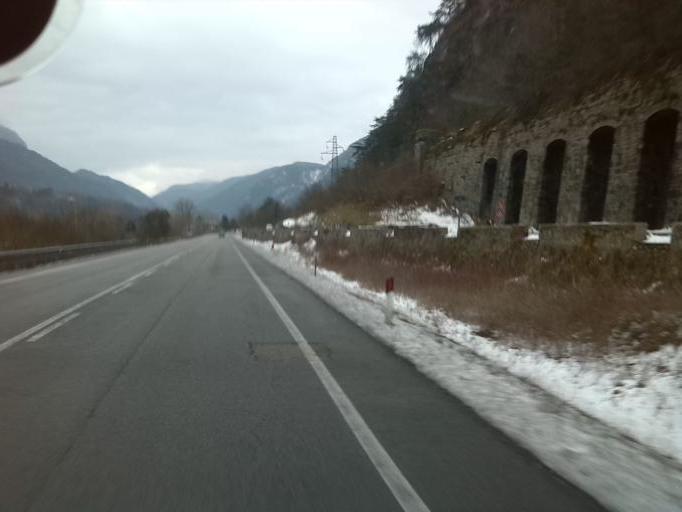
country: IT
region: Friuli Venezia Giulia
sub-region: Provincia di Udine
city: Resiutta
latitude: 46.3956
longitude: 13.2060
